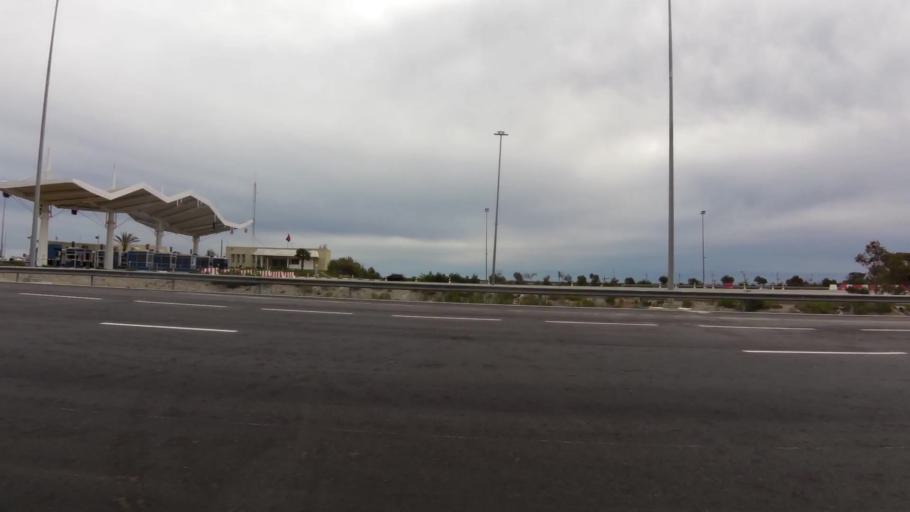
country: MA
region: Tanger-Tetouan
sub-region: Tetouan
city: Martil
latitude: 35.7436
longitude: -5.3540
